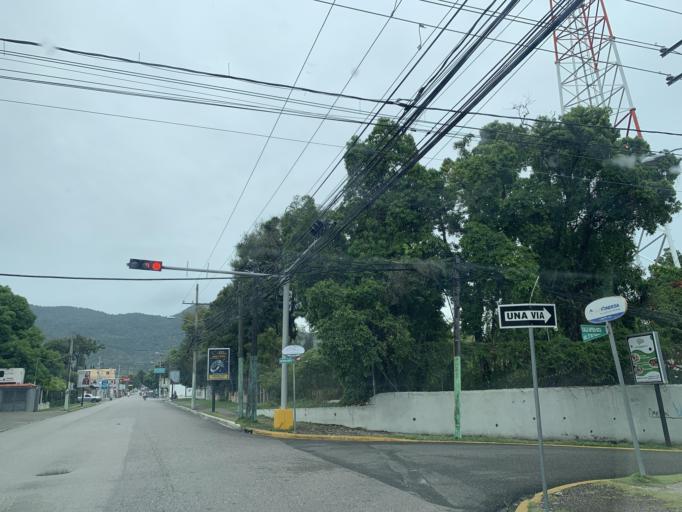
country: DO
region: Puerto Plata
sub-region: Puerto Plata
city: Puerto Plata
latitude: 19.7928
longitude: -70.6862
